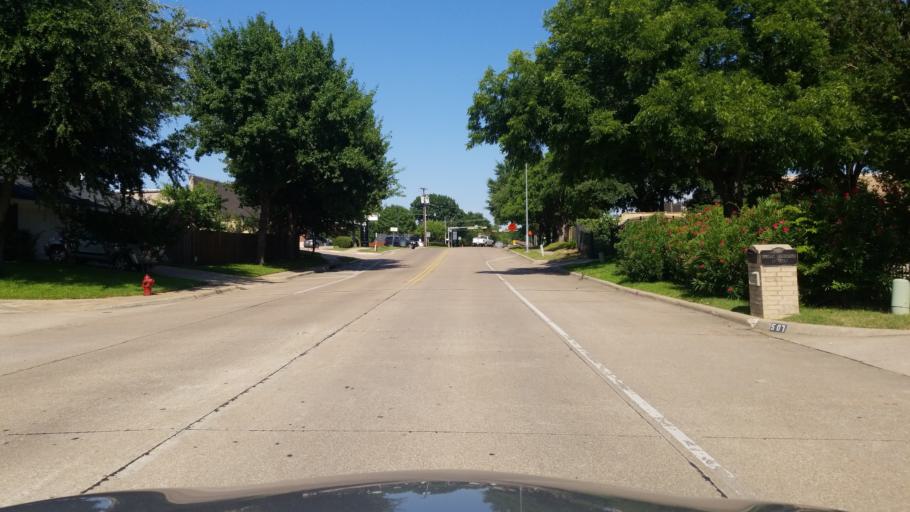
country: US
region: Texas
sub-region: Dallas County
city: Grand Prairie
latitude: 32.6805
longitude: -97.0090
